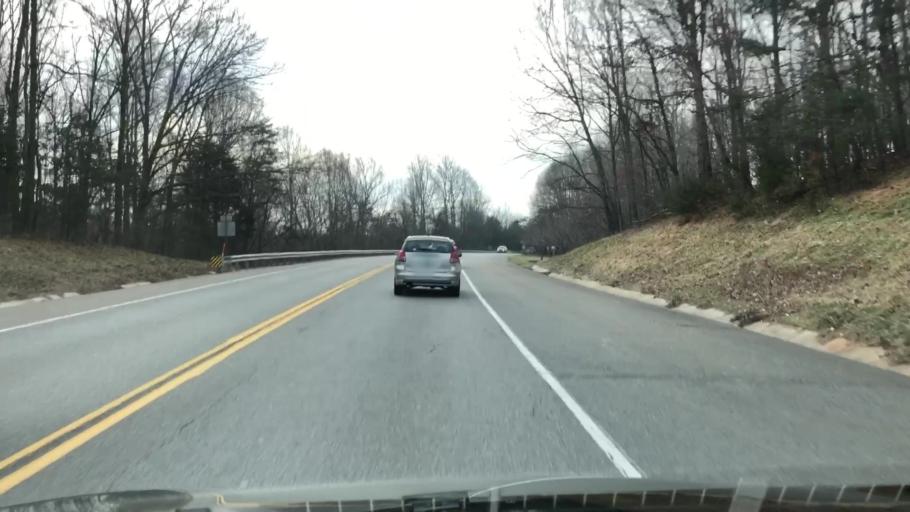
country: US
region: Virginia
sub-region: City of Lynchburg
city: West Lynchburg
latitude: 37.4230
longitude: -79.2319
